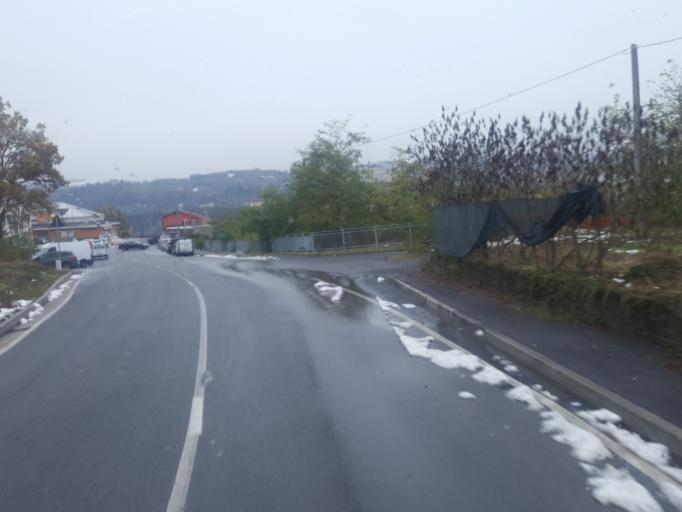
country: IT
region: Piedmont
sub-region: Provincia di Cuneo
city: Breo
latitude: 44.4039
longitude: 7.8270
